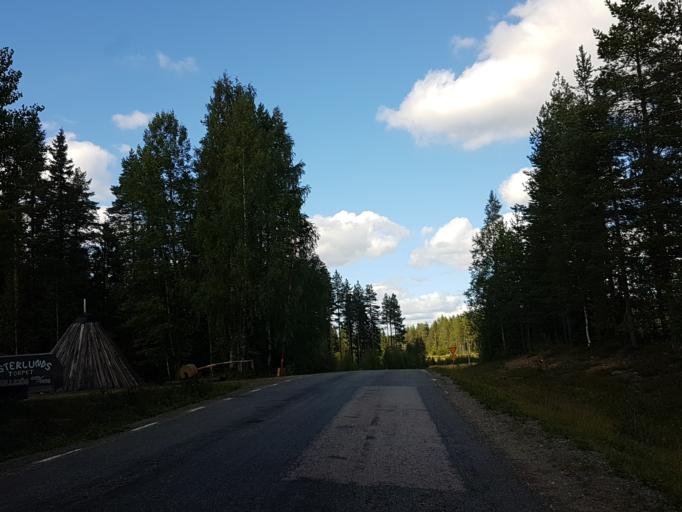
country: SE
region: Vaesterbotten
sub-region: Skelleftea Kommun
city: Burtraesk
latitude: 64.2616
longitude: 20.4770
